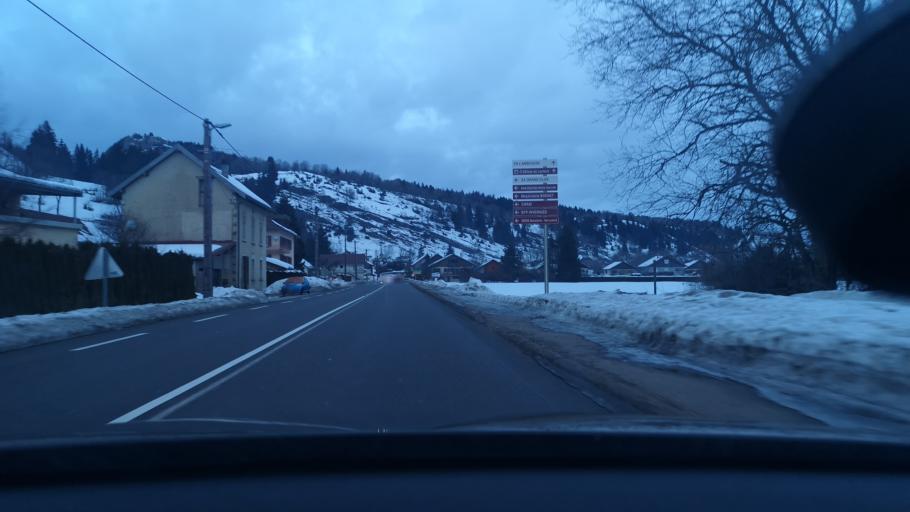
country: FR
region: Franche-Comte
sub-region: Departement du Doubs
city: La Cluse-et-Mijoux
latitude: 46.8680
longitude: 6.3746
